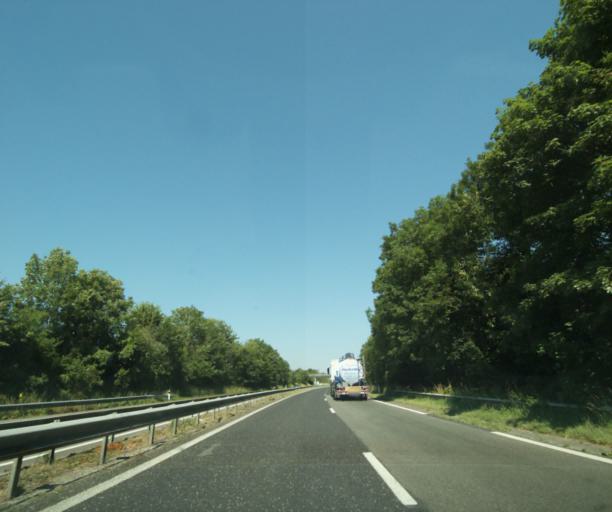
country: FR
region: Lorraine
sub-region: Departement de la Meuse
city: Longeville-en-Barrois
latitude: 48.6454
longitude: 5.1818
